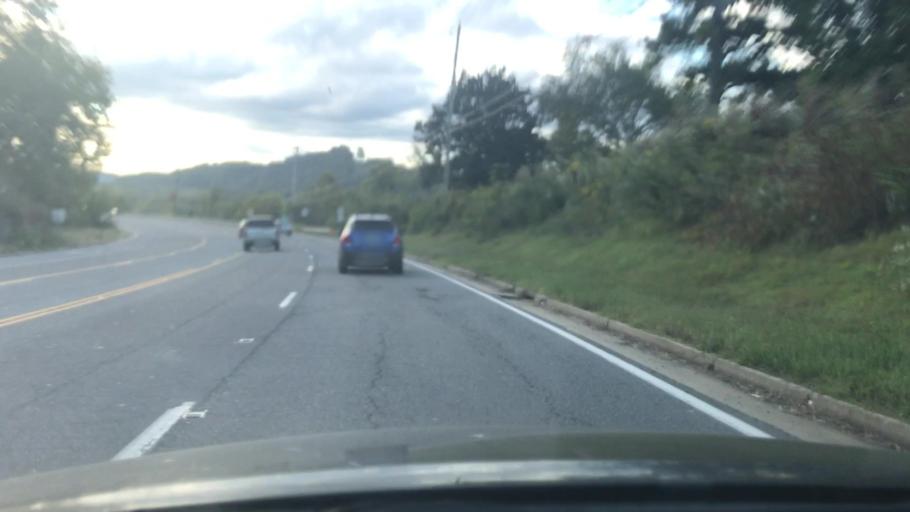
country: US
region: Tennessee
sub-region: Cheatham County
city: Ashland City
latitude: 36.2640
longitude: -87.0585
